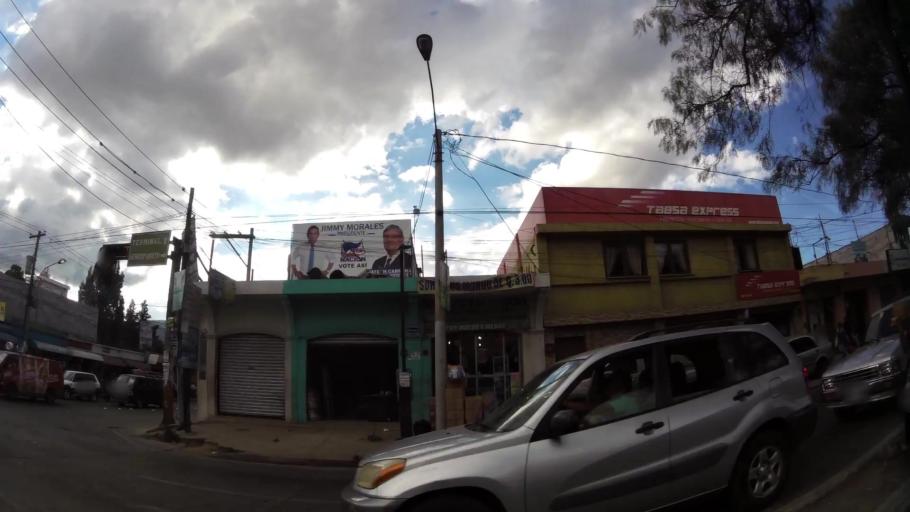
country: GT
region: Quetzaltenango
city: Quetzaltenango
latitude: 14.8475
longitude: -91.5228
